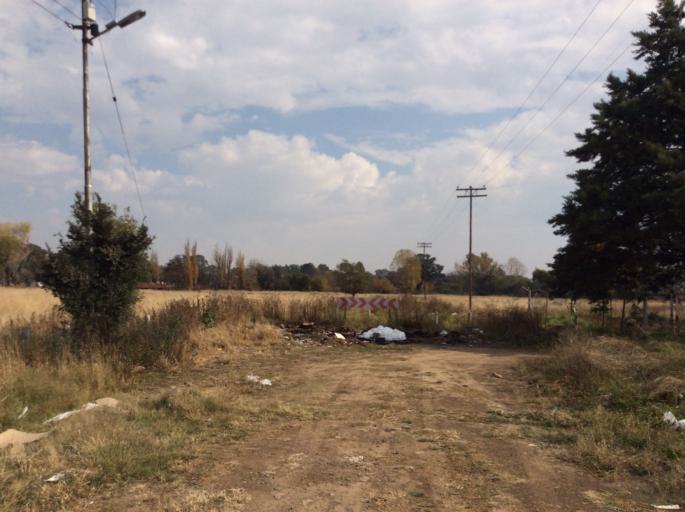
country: LS
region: Mafeteng
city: Mafeteng
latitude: -29.7304
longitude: 27.0364
